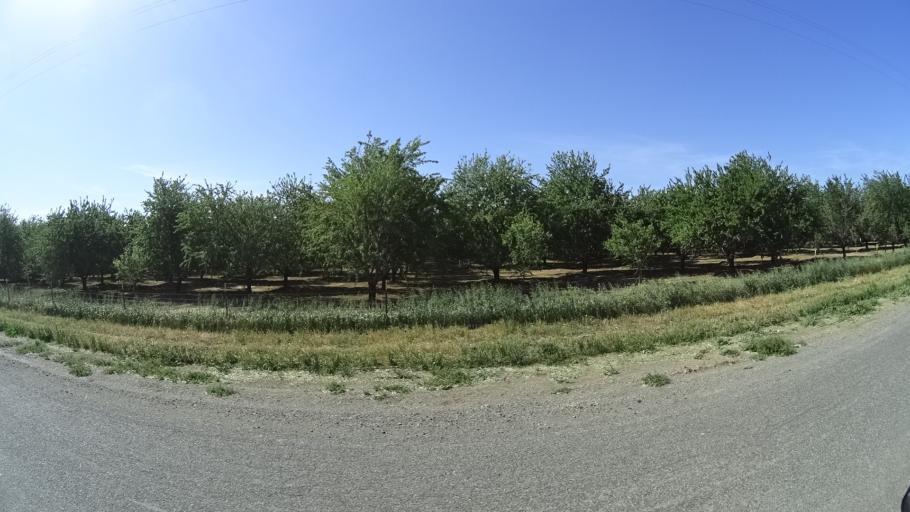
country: US
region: California
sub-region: Glenn County
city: Orland
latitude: 39.6530
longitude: -122.1650
